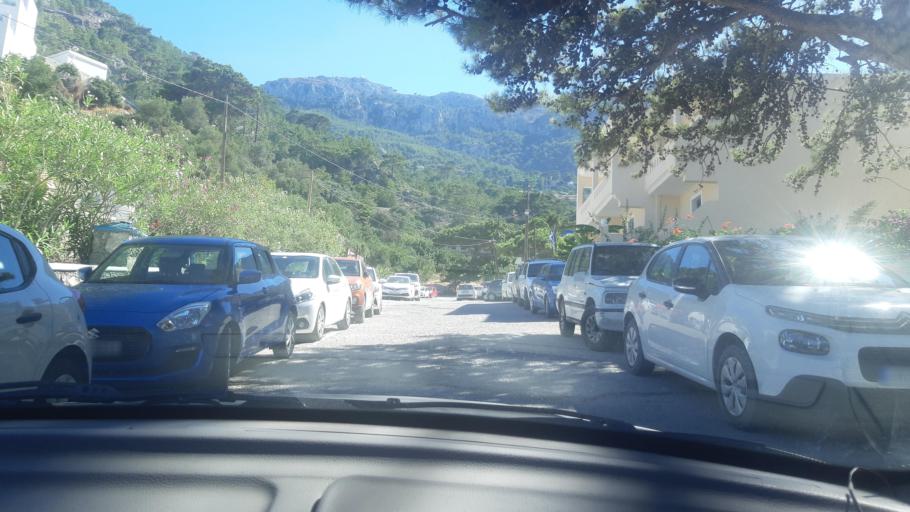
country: GR
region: South Aegean
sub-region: Nomos Dodekanisou
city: Karpathos
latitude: 35.5870
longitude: 27.1775
